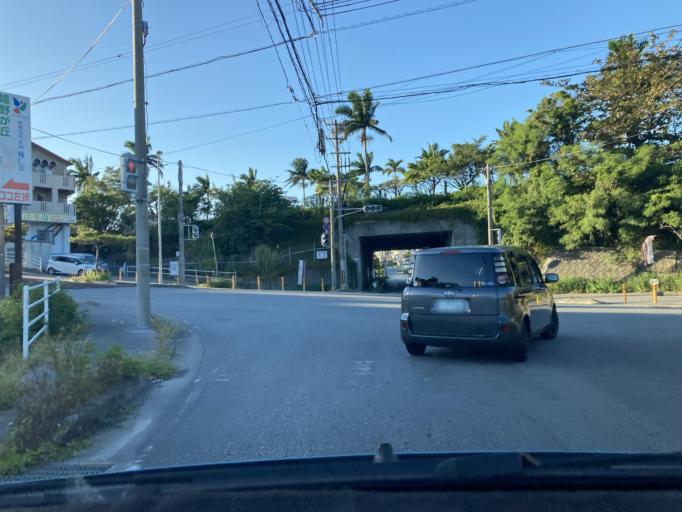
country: JP
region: Okinawa
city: Naha-shi
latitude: 26.2119
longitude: 127.7296
